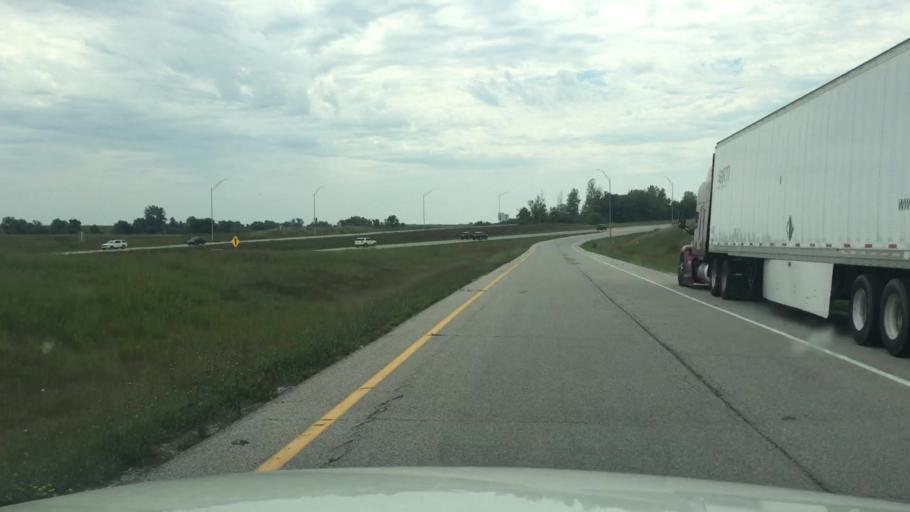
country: US
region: Iowa
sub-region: Decatur County
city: Lamoni
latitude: 40.6226
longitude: -93.8932
